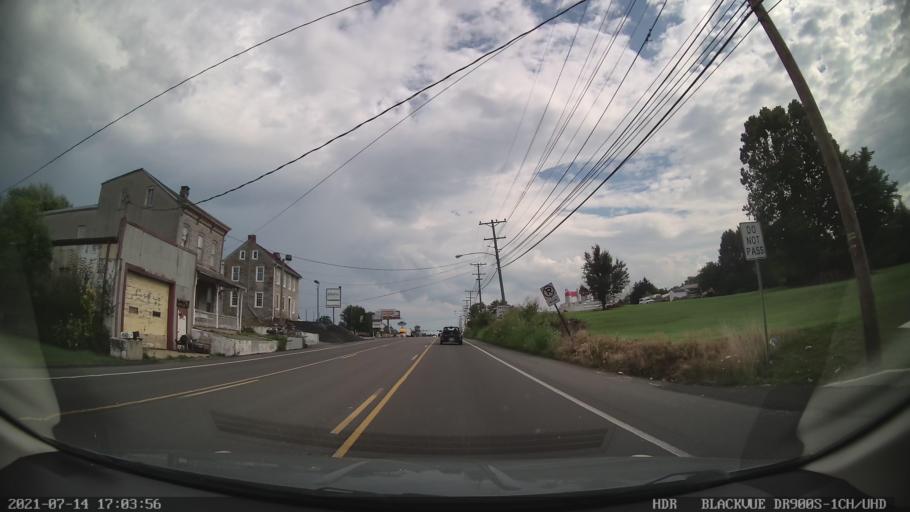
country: US
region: Pennsylvania
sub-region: Berks County
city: Muhlenberg Park
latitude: 40.3879
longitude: -75.9348
